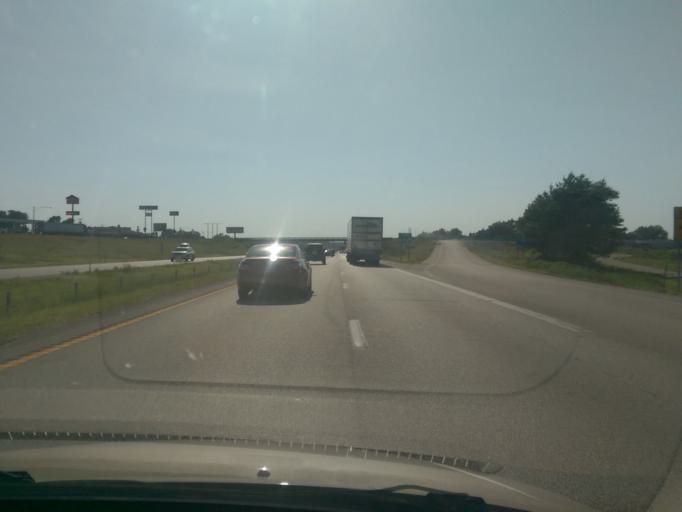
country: US
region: Missouri
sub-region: Saline County
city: Sweet Springs
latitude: 38.9771
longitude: -93.4121
